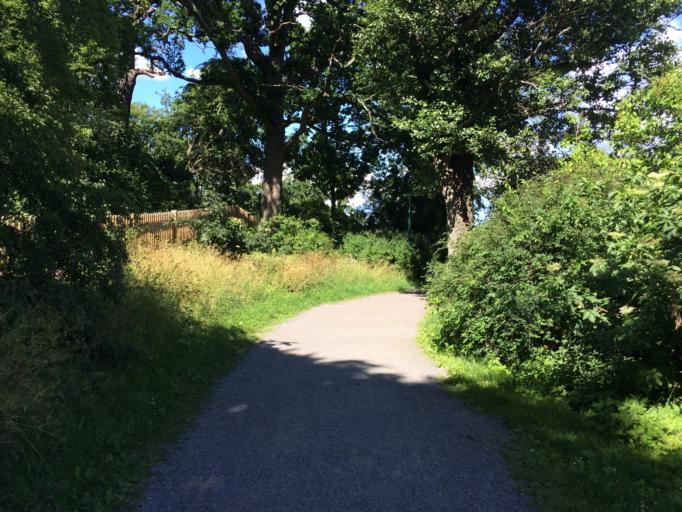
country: SE
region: Stockholm
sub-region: Nacka Kommun
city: Nacka
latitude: 59.3252
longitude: 18.1491
